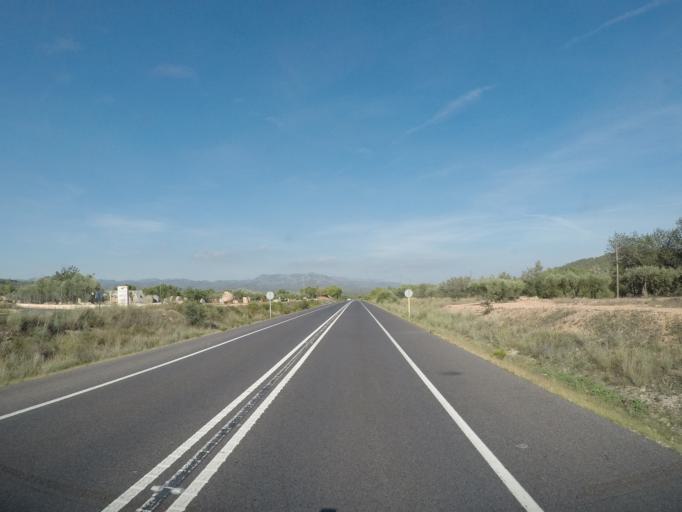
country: ES
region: Catalonia
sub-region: Provincia de Tarragona
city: El Perello
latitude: 40.8888
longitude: 0.7212
